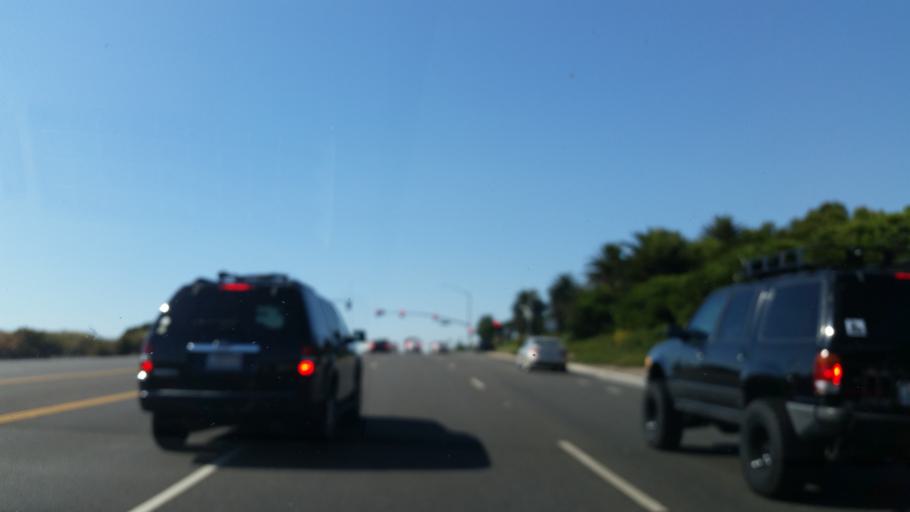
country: US
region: California
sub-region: Orange County
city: San Joaquin Hills
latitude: 33.5663
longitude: -117.8291
